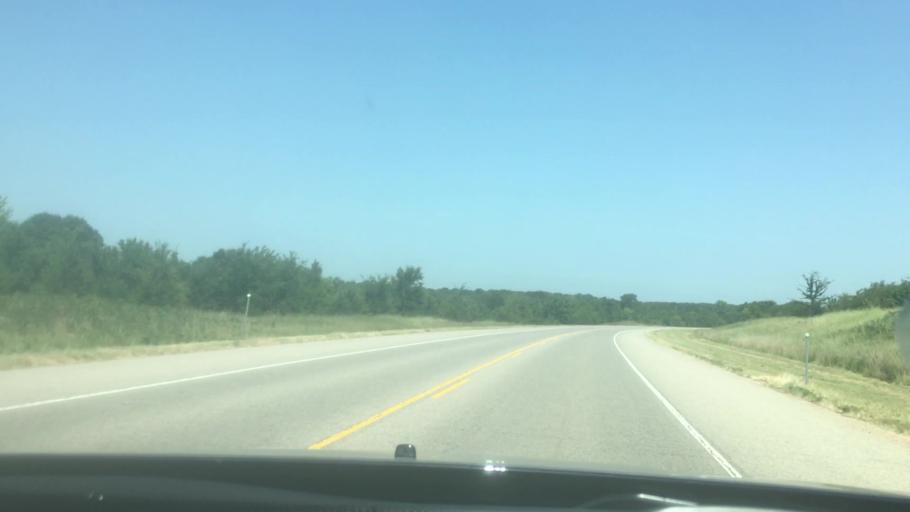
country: US
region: Oklahoma
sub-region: Pontotoc County
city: Ada
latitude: 34.6454
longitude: -96.5481
